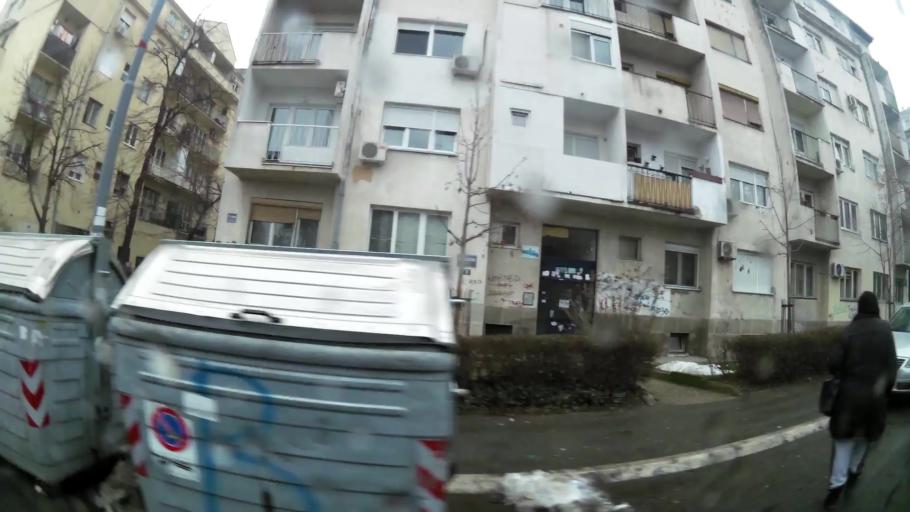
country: RS
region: Central Serbia
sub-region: Belgrade
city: Cukarica
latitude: 44.7823
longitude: 20.4165
